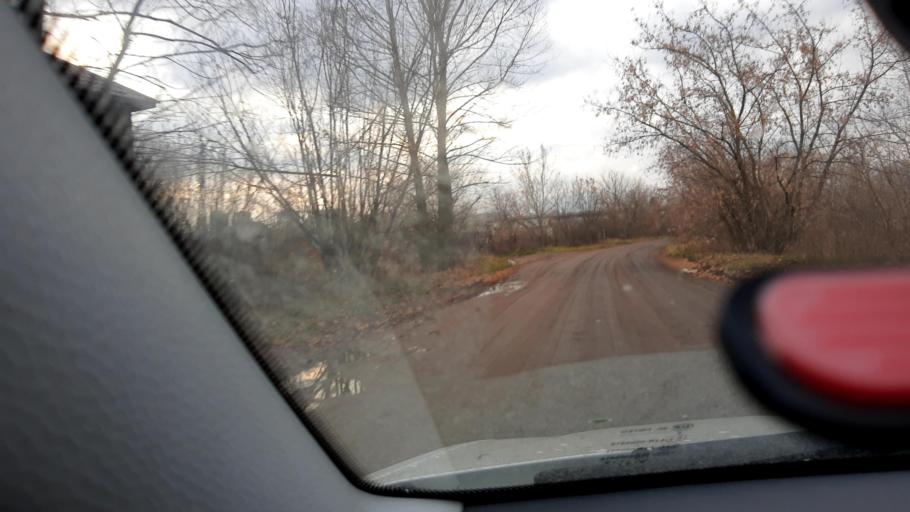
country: RU
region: Bashkortostan
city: Mikhaylovka
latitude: 54.7070
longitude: 55.8649
